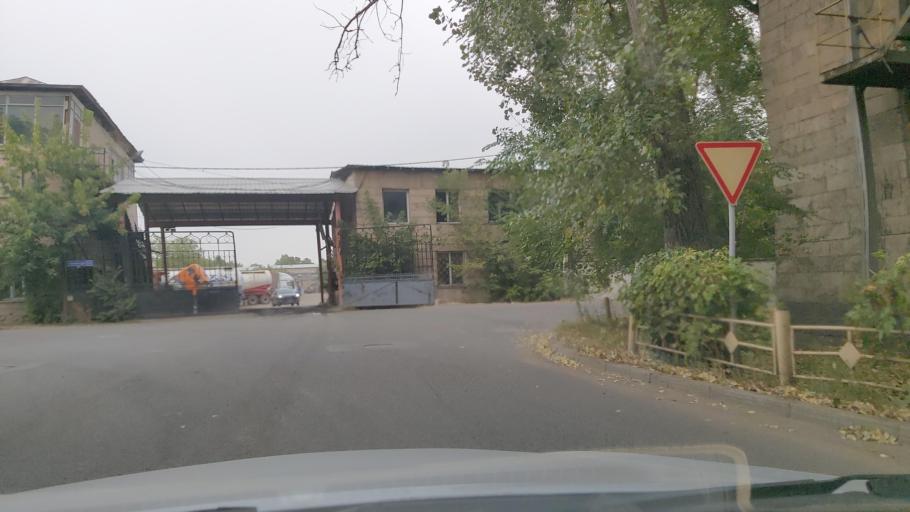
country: KZ
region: Almaty Oblysy
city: Pervomayskiy
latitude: 43.3545
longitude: 76.9806
